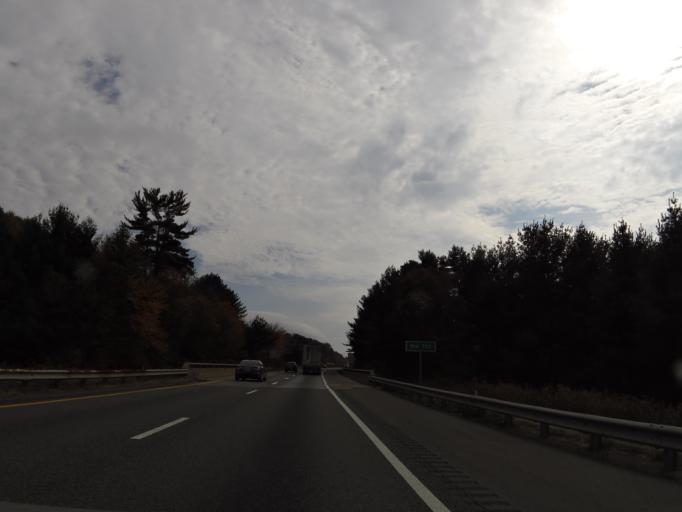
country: US
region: Virginia
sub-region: Carroll County
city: Hillsville
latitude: 36.7190
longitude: -80.7466
